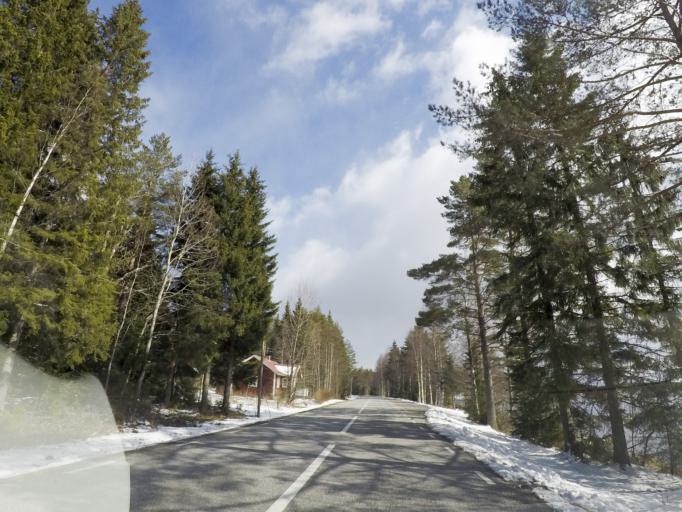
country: SE
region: OErebro
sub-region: Lindesbergs Kommun
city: Stora
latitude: 59.9006
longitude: 15.2136
